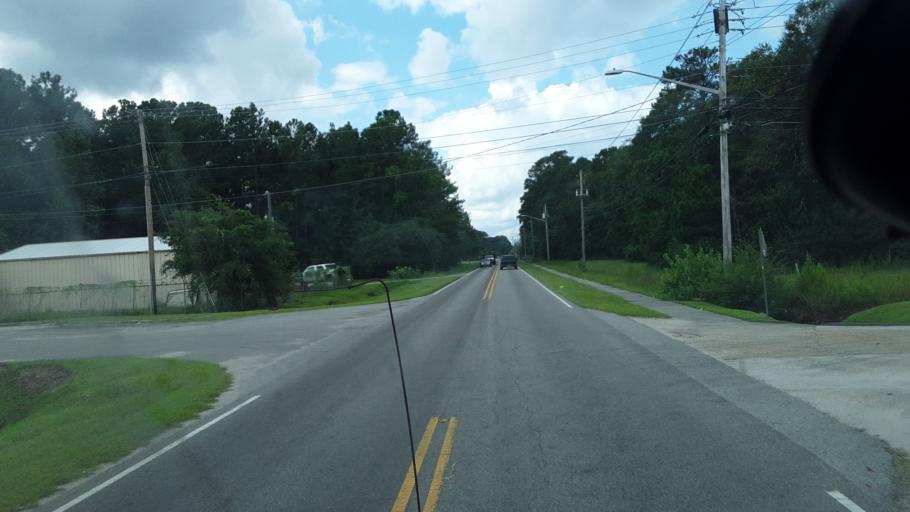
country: US
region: South Carolina
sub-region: Georgetown County
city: Georgetown
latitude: 33.3890
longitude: -79.2912
